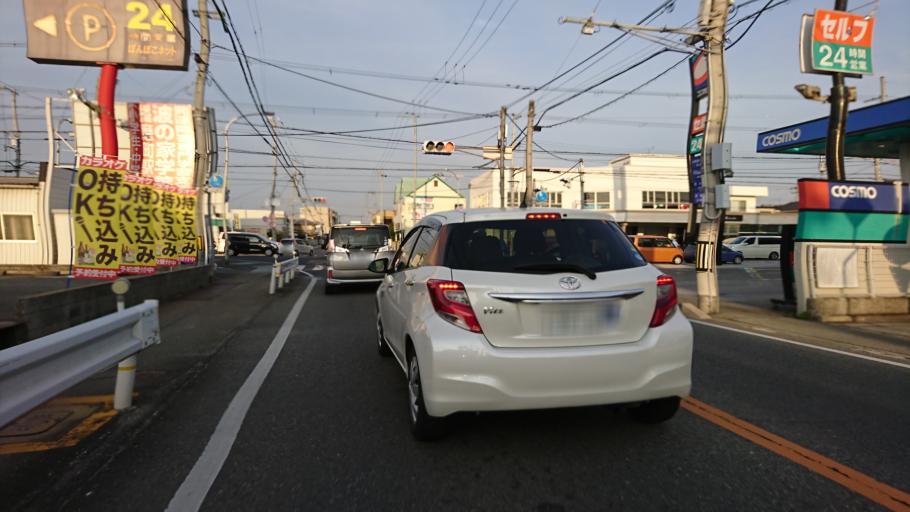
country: JP
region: Hyogo
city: Kakogawacho-honmachi
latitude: 34.7458
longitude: 134.8636
